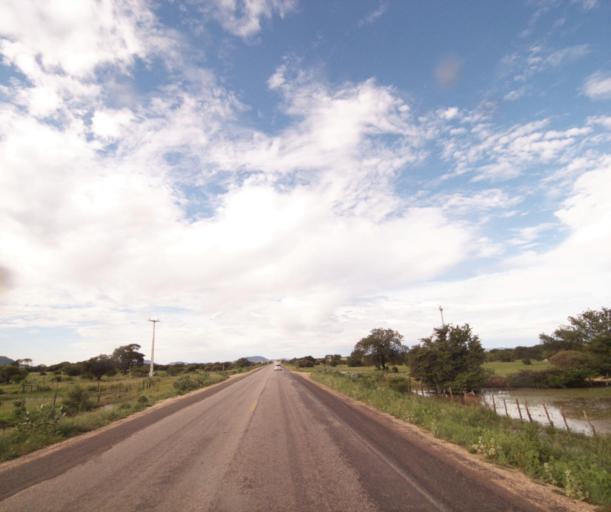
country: BR
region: Bahia
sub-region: Guanambi
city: Guanambi
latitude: -14.2855
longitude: -42.7840
